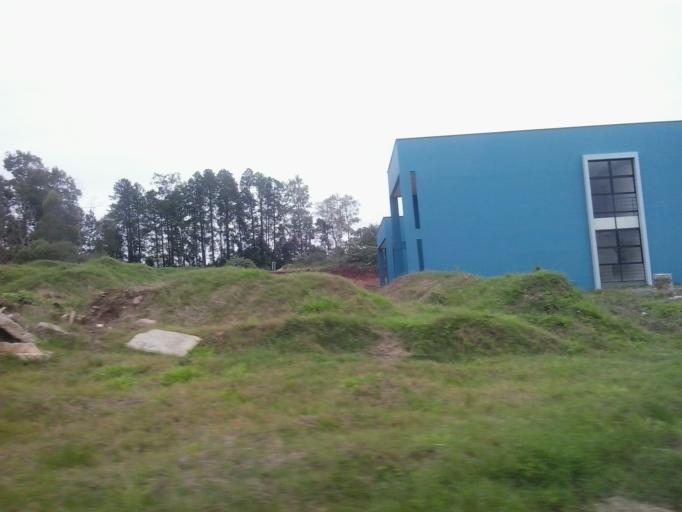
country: BR
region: Rio Grande do Sul
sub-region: Santa Maria
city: Santa Maria
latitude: -29.7124
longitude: -53.7192
